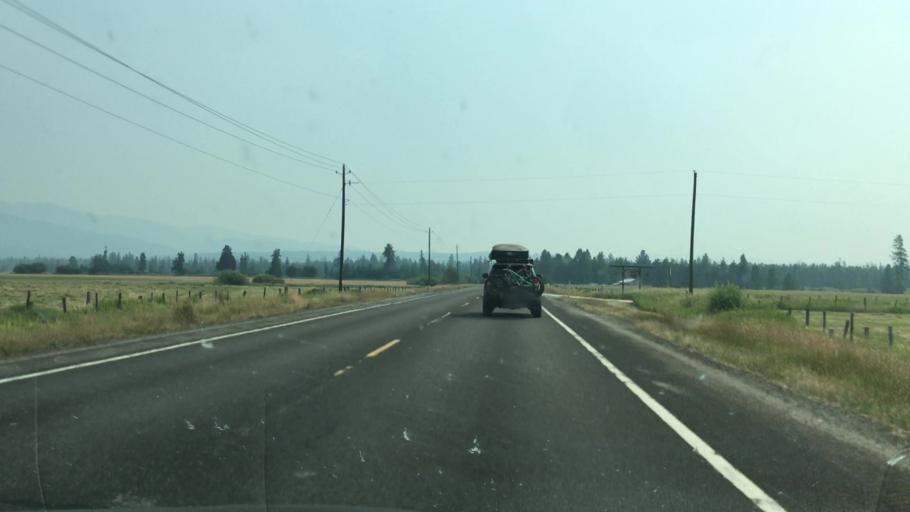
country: US
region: Idaho
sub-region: Valley County
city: Cascade
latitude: 44.4186
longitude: -115.9997
